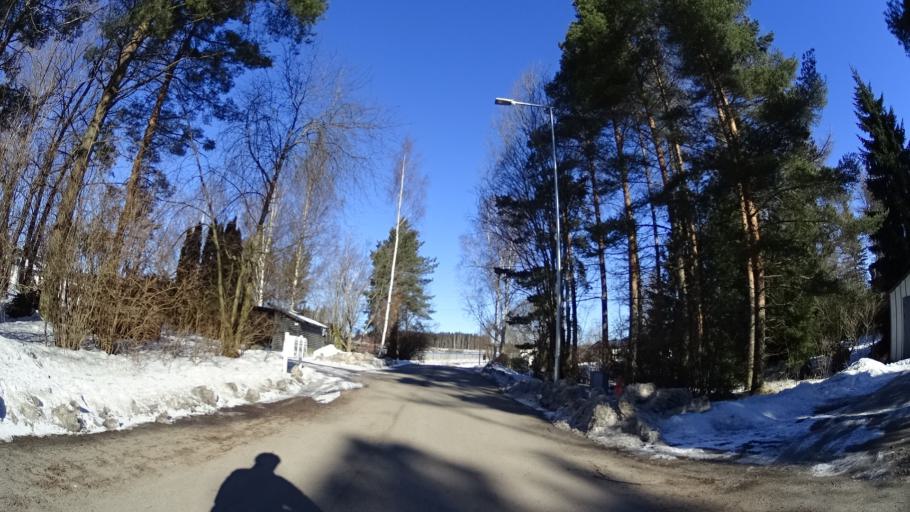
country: FI
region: Uusimaa
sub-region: Helsinki
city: Kilo
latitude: 60.2880
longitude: 24.8421
